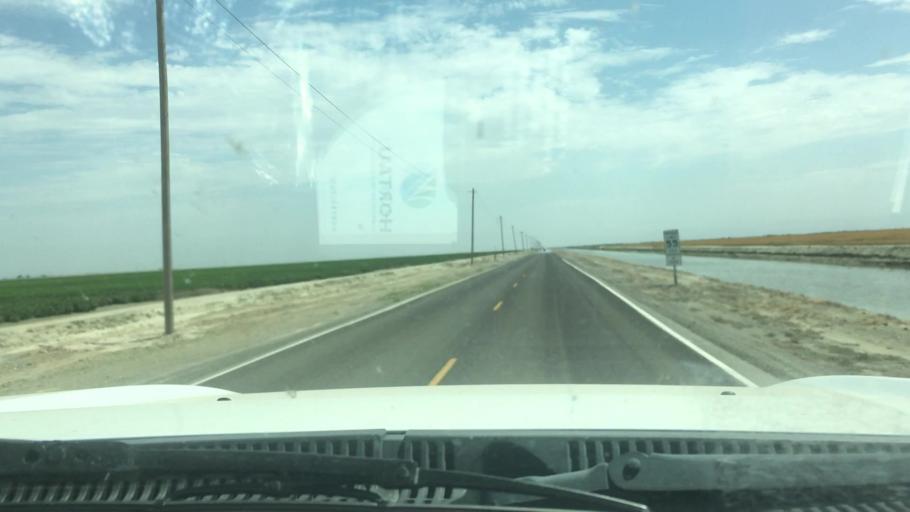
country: US
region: California
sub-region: Tulare County
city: Alpaugh
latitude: 35.8888
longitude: -119.5735
